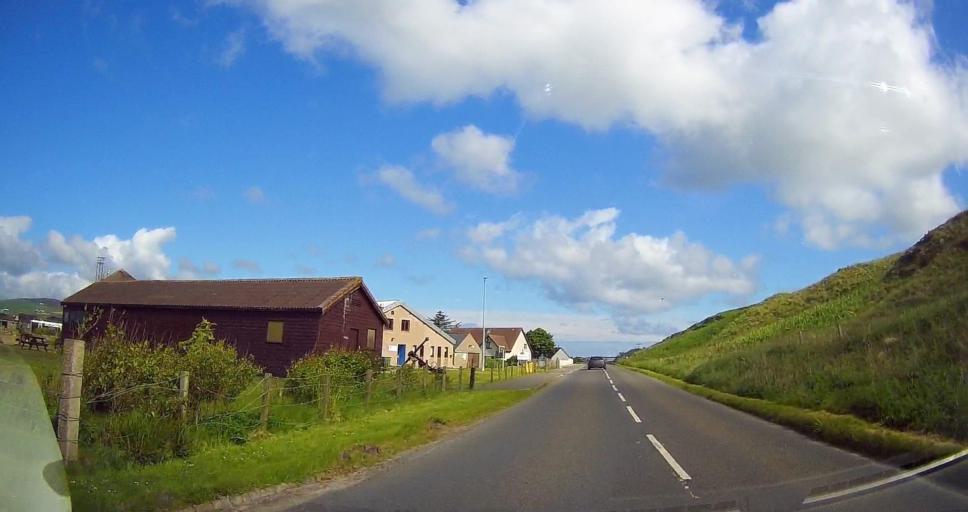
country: GB
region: Scotland
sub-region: Orkney Islands
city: Orkney
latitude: 58.9601
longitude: -2.9688
